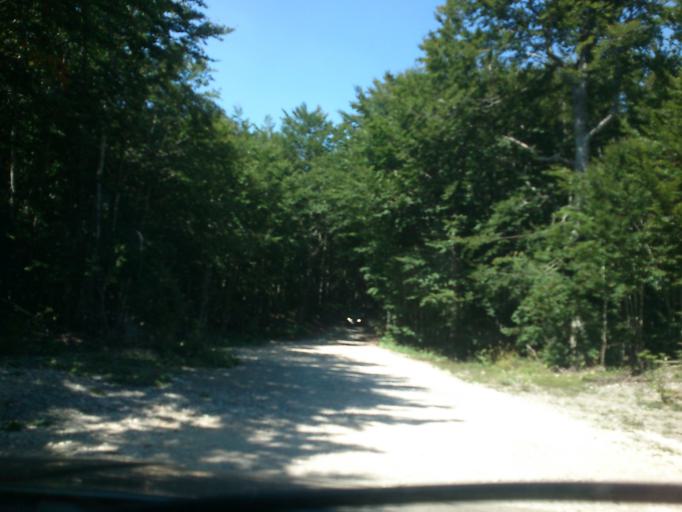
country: HR
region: Licko-Senjska
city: Senj
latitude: 44.8271
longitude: 14.9794
